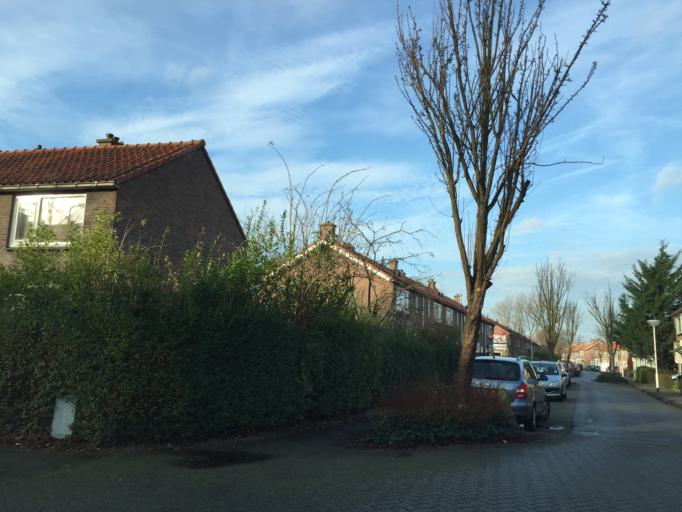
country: NL
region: South Holland
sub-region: Gemeente Zoetermeer
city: Zoetermeer
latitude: 52.0507
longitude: 4.5061
